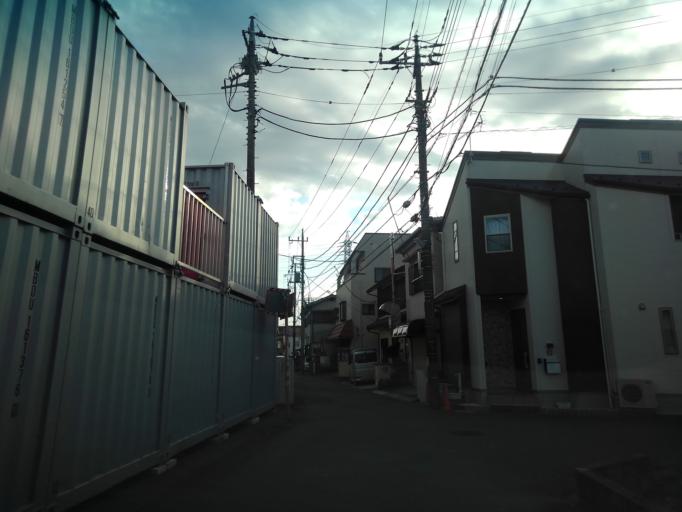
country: JP
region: Saitama
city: Tokorozawa
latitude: 35.7902
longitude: 139.4414
